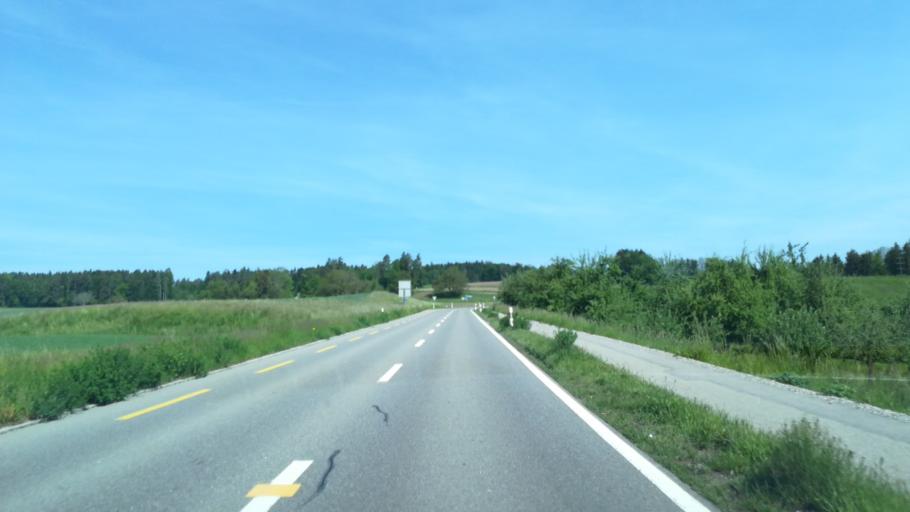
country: CH
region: Thurgau
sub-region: Frauenfeld District
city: Pfyn
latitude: 47.6023
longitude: 8.9469
